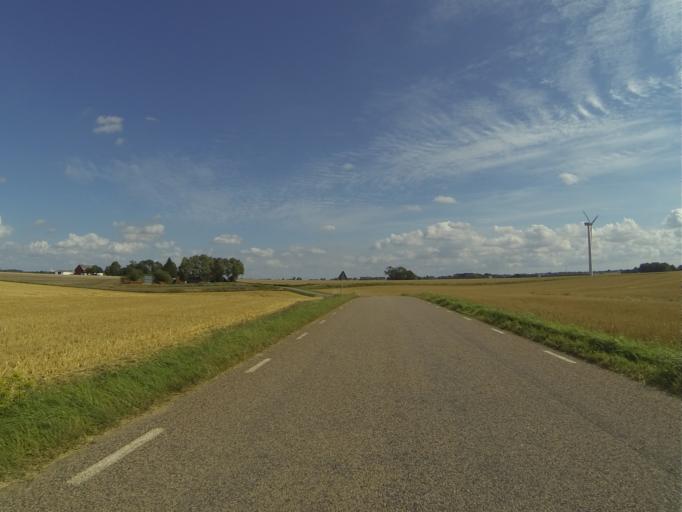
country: SE
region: Skane
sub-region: Kavlinge Kommun
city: Kaevlinge
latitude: 55.7809
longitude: 13.1794
